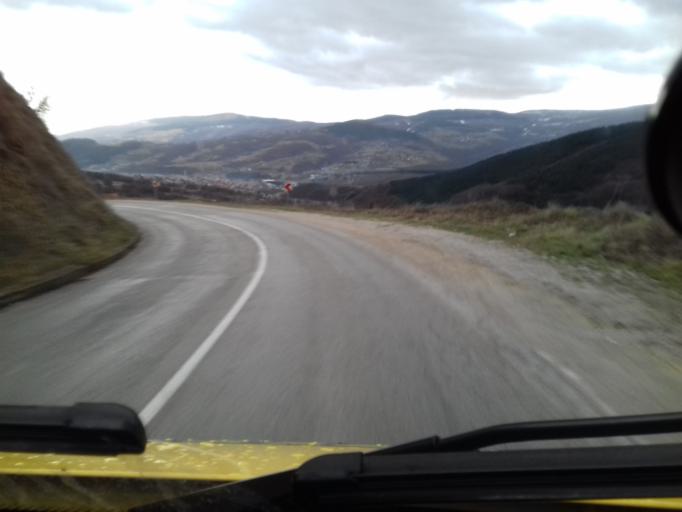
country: BA
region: Federation of Bosnia and Herzegovina
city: Turbe
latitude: 44.2618
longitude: 17.5417
